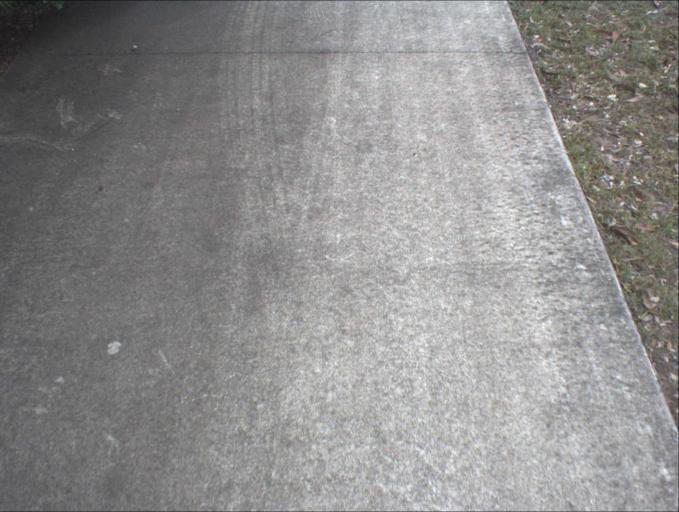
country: AU
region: Queensland
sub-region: Logan
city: Logan Reserve
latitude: -27.7083
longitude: 153.0754
